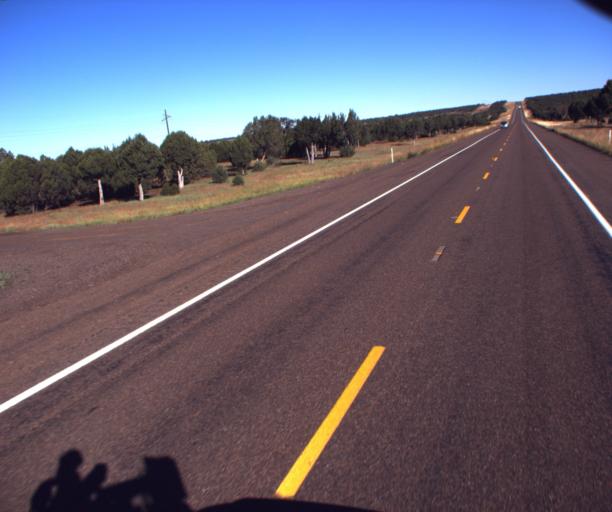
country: US
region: Arizona
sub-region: Navajo County
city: White Mountain Lake
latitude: 34.3175
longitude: -110.0417
